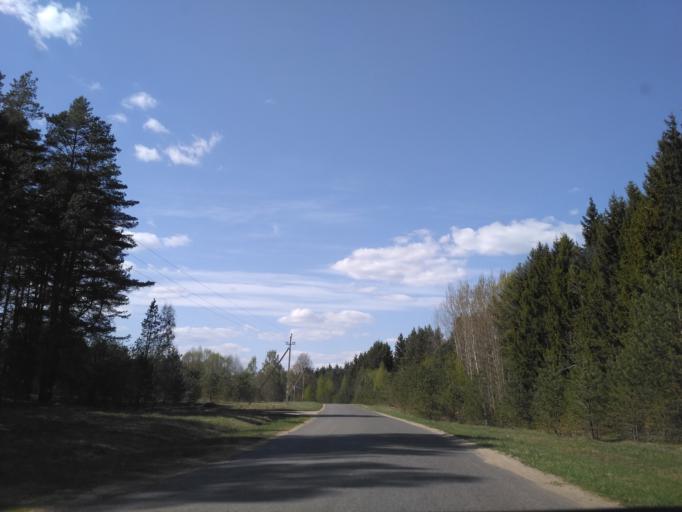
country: BY
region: Minsk
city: Narach
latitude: 54.9607
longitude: 26.6486
